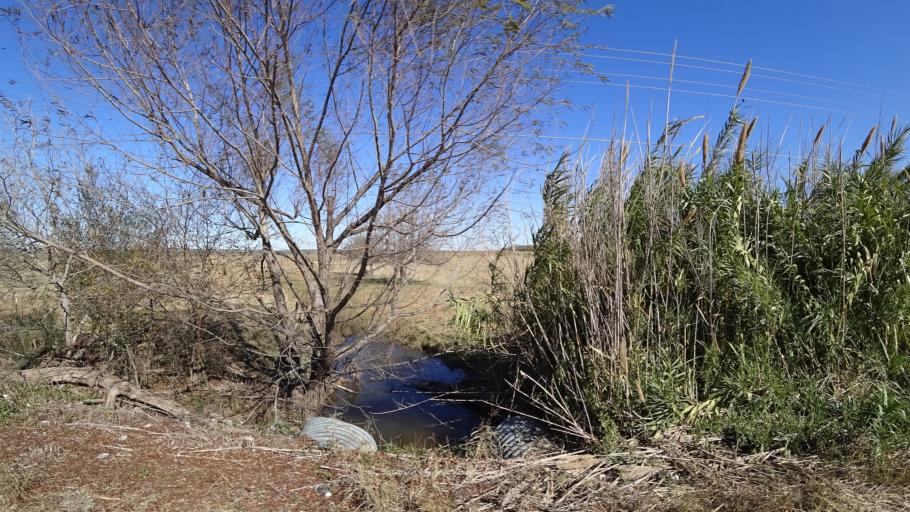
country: US
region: Texas
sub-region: Travis County
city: Garfield
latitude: 30.1148
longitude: -97.5883
